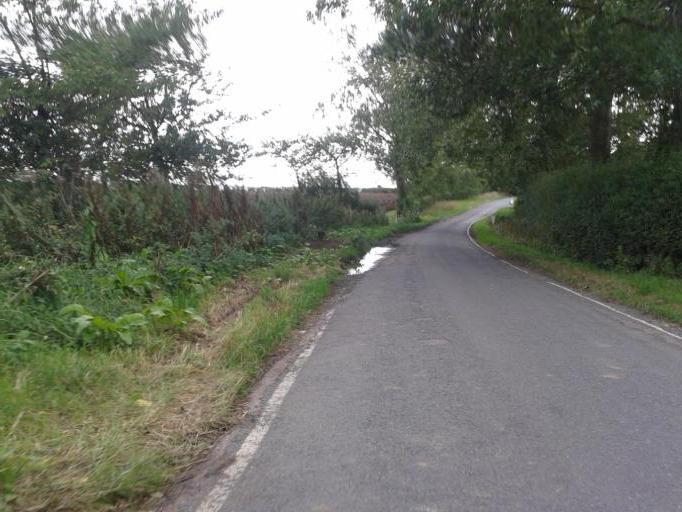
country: GB
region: England
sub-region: Cambridgeshire
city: Duxford
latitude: 52.0001
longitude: 0.1109
